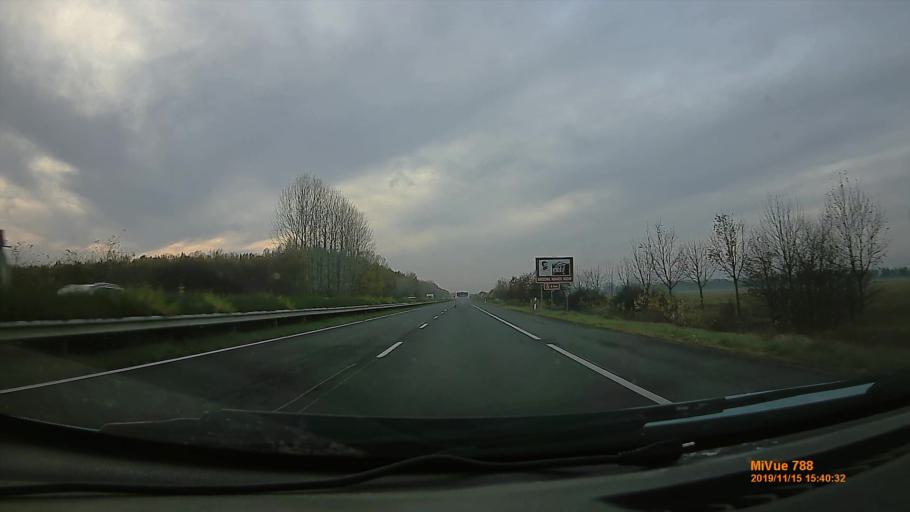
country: HU
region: Bekes
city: Bekescsaba
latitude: 46.6745
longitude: 21.1501
